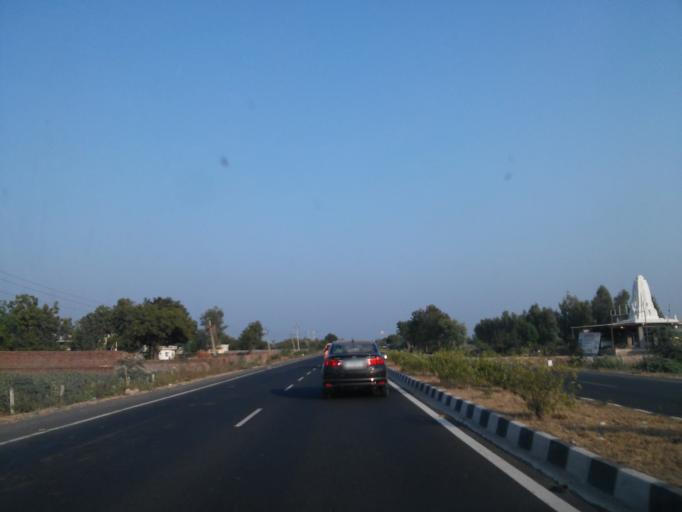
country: IN
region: Gujarat
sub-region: Ahmadabad
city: Mandal
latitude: 23.0976
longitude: 72.0992
